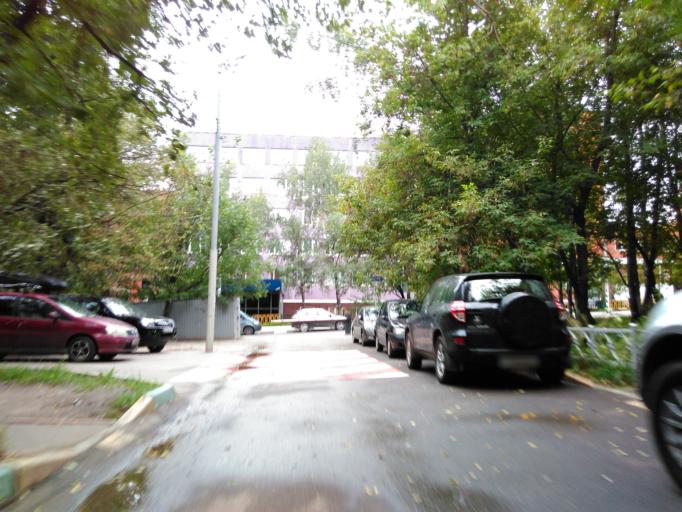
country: RU
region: Moskovskaya
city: Cheremushki
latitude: 55.6745
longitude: 37.5790
